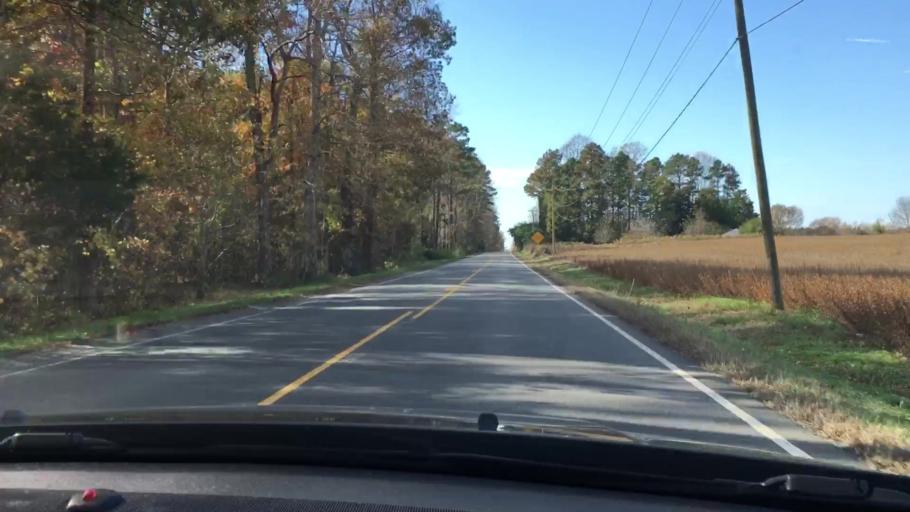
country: US
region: Virginia
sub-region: King and Queen County
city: King and Queen Court House
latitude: 37.5914
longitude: -76.8656
